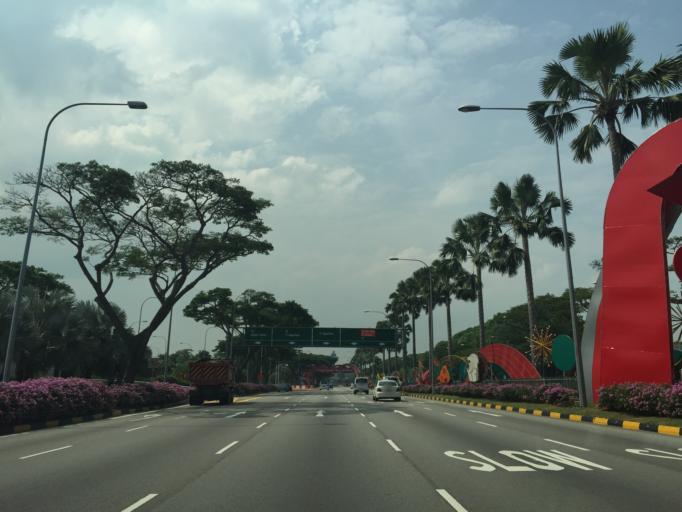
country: SG
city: Singapore
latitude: 1.3471
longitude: 103.9841
